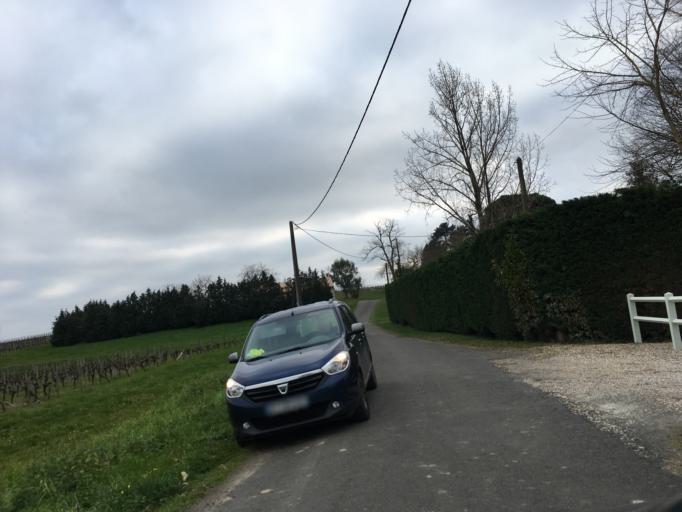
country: FR
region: Aquitaine
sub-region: Departement de la Gironde
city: Saint-Ciers-sur-Gironde
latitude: 45.3082
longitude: -0.6042
